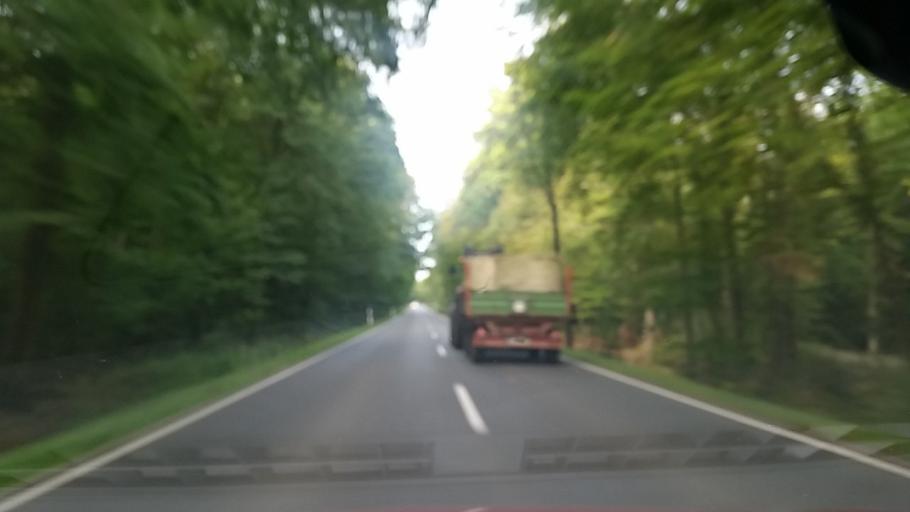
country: DE
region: Lower Saxony
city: Wienhausen
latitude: 52.6278
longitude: 10.1837
